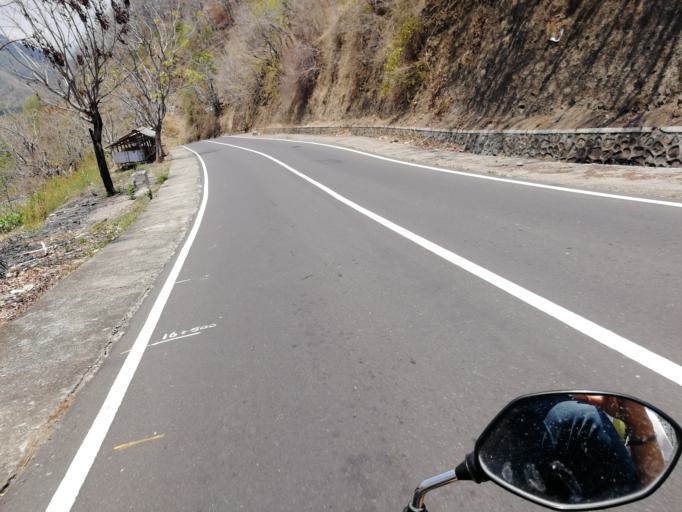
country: ID
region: West Nusa Tenggara
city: Karangsubagan
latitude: -8.4438
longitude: 116.0351
